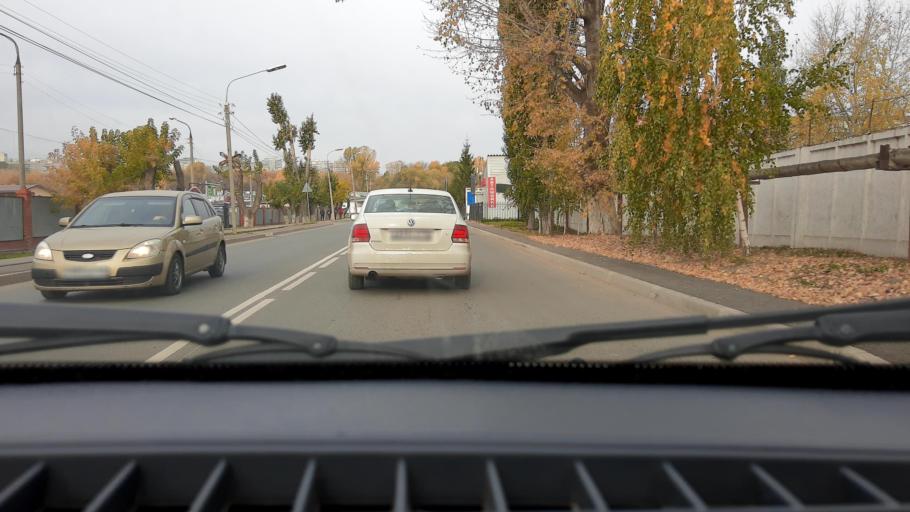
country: RU
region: Bashkortostan
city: Ufa
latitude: 54.7876
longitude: 56.0599
